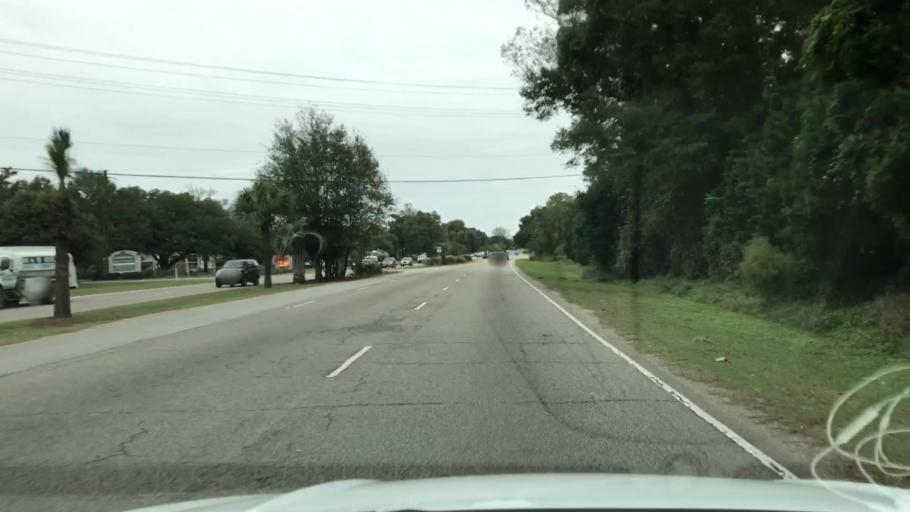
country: US
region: South Carolina
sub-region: Georgetown County
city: Murrells Inlet
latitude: 33.4781
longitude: -79.1006
